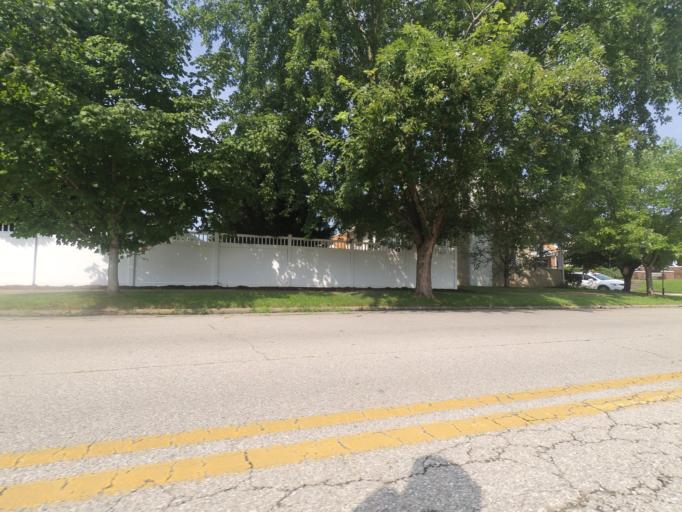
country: US
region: West Virginia
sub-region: Cabell County
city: Huntington
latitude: 38.4078
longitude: -82.4538
